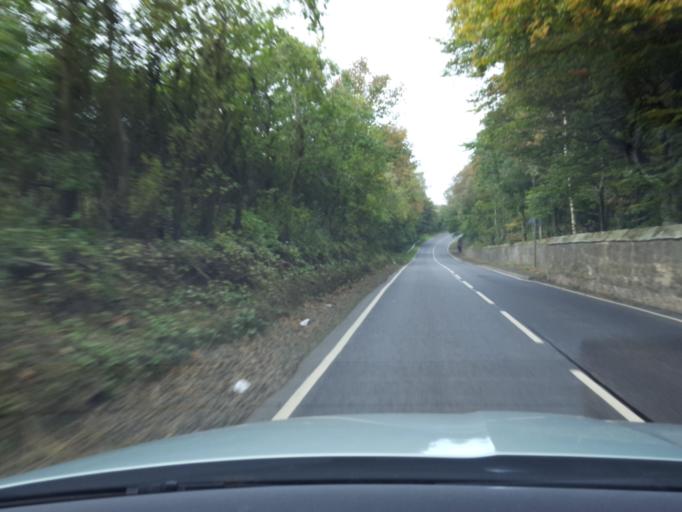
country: GB
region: Scotland
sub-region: Fife
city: Pathhead
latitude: 55.8583
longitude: -3.0000
